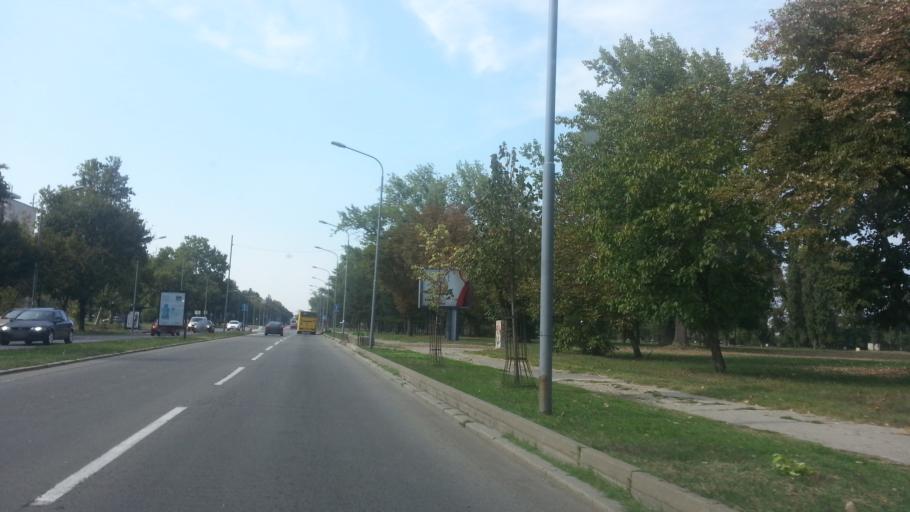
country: RS
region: Central Serbia
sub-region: Belgrade
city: Novi Beograd
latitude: 44.8200
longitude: 20.4323
